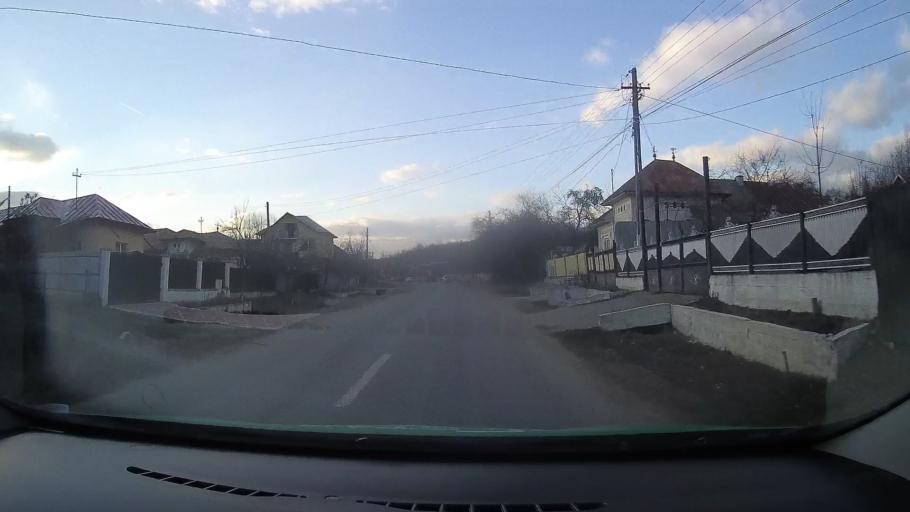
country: RO
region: Dambovita
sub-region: Comuna Gura Ocnitei
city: Adanca
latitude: 44.9324
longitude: 25.5989
